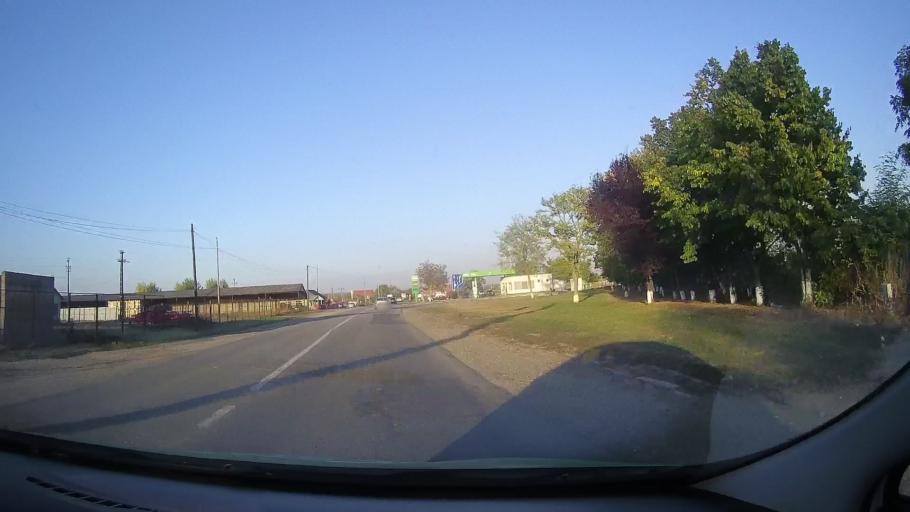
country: RO
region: Bihor
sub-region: Comuna Salard
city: Salard
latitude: 47.2106
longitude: 22.0218
